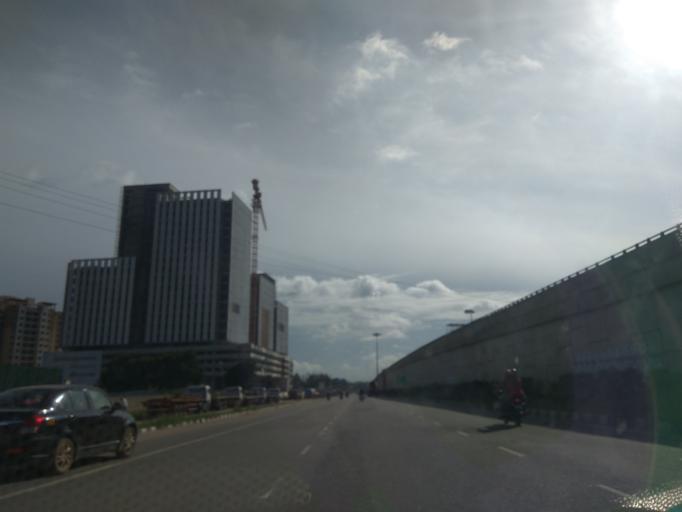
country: IN
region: Karnataka
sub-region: Bangalore Rural
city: Hoskote
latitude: 13.0525
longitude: 77.7600
